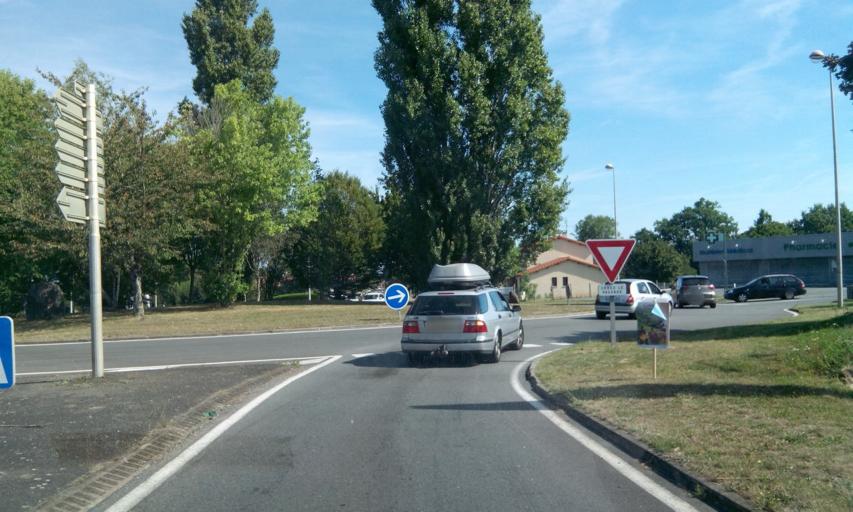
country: FR
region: Poitou-Charentes
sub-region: Departement de la Charente
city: Confolens
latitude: 46.0032
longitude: 0.6740
